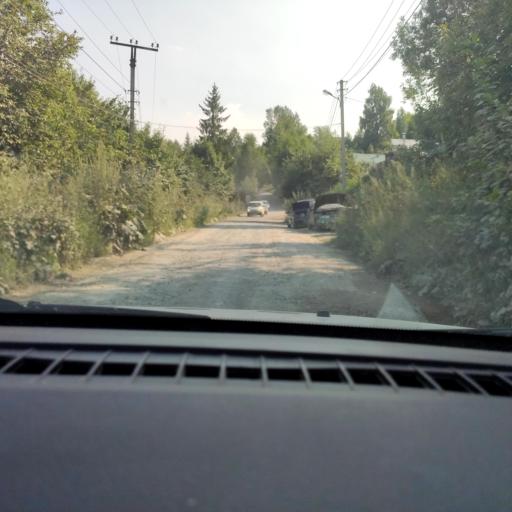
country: RU
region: Perm
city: Polazna
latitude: 58.1419
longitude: 56.4568
